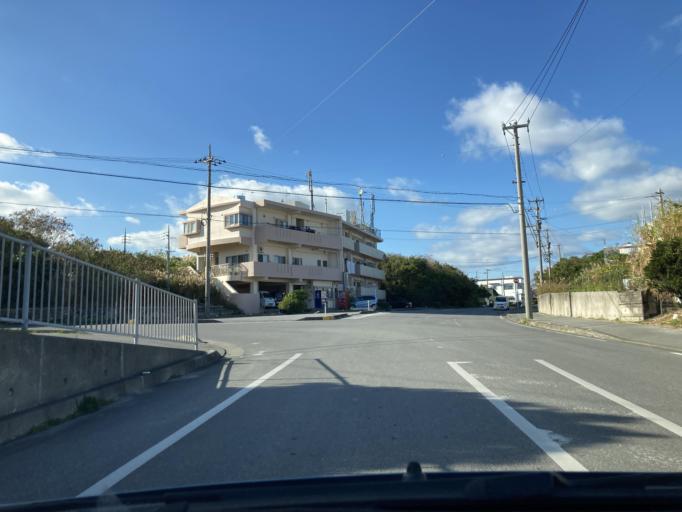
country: JP
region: Okinawa
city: Katsuren-haebaru
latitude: 26.3052
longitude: 127.9154
